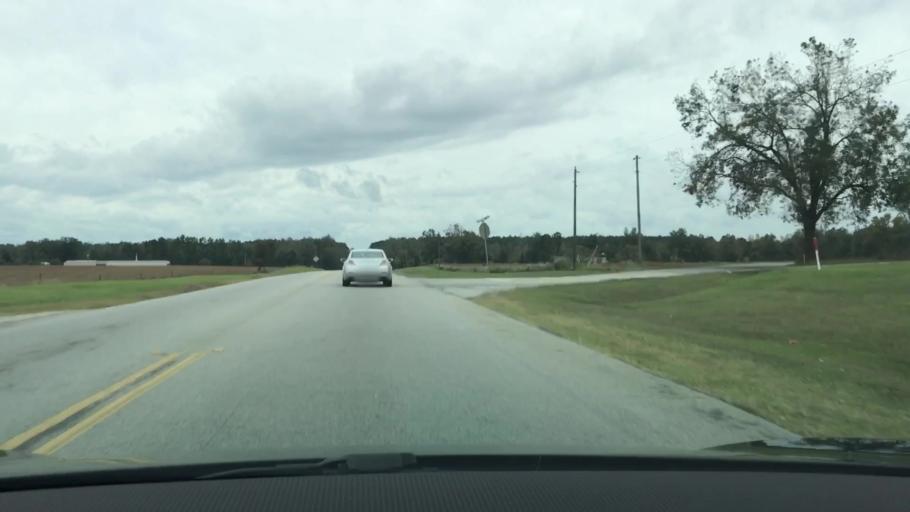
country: US
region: Georgia
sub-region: Jefferson County
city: Louisville
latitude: 32.9486
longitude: -82.3946
